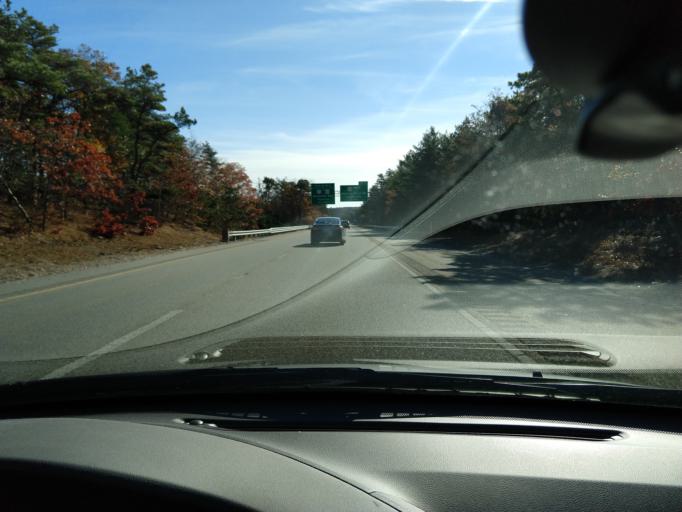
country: US
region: Massachusetts
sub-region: Barnstable County
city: Sagamore
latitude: 41.8201
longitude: -70.5571
